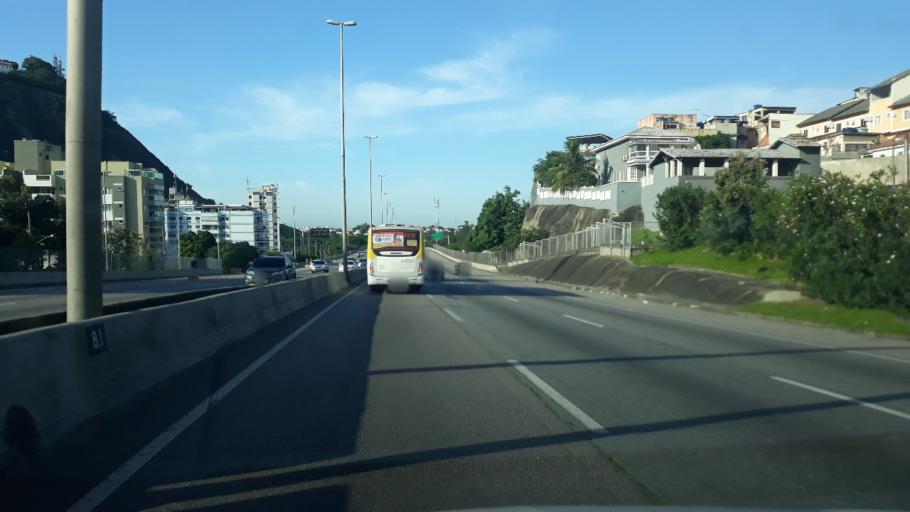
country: BR
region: Rio de Janeiro
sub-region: Sao Joao De Meriti
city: Sao Joao de Meriti
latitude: -22.9356
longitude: -43.3470
